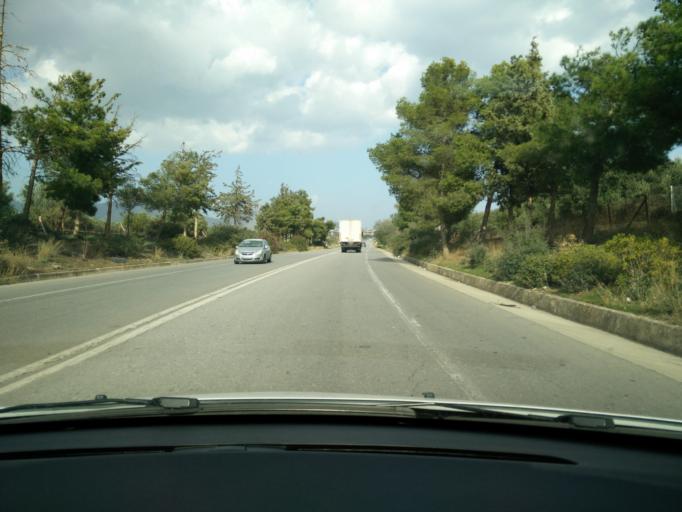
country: GR
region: Crete
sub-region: Nomos Lasithiou
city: Agios Nikolaos
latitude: 35.1941
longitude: 25.7030
